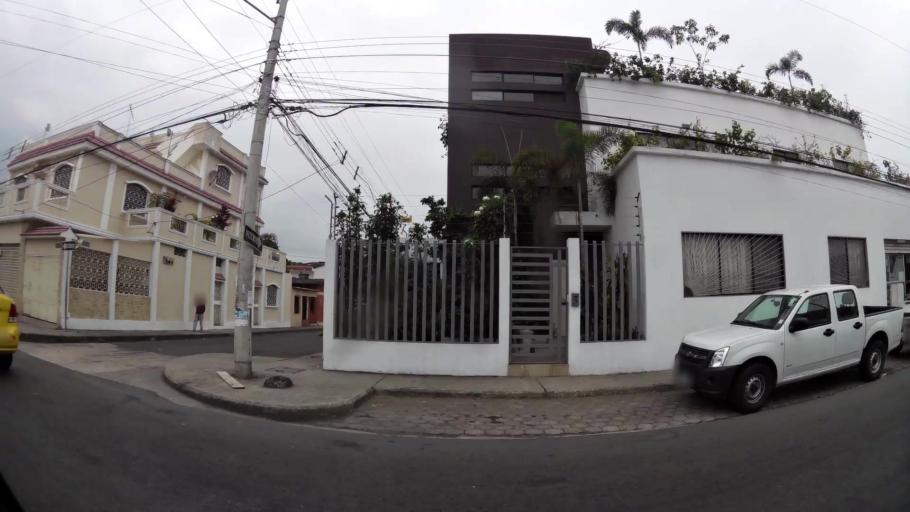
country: EC
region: Guayas
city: Eloy Alfaro
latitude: -2.1366
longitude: -79.8990
